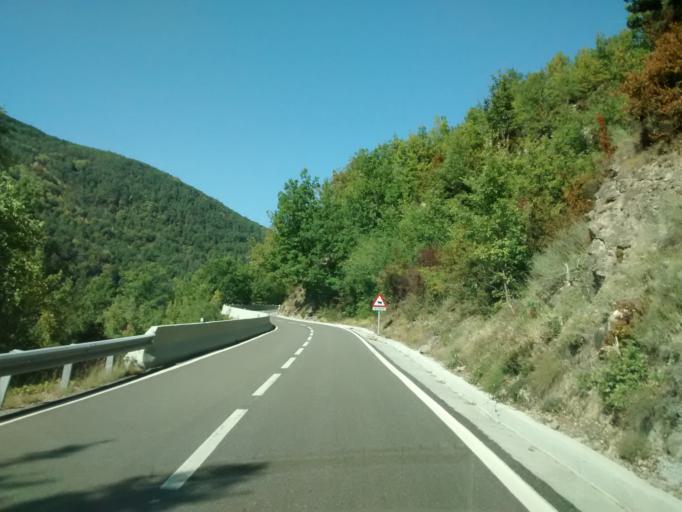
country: ES
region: Aragon
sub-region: Provincia de Huesca
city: Fiscal
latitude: 42.5296
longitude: -0.1345
